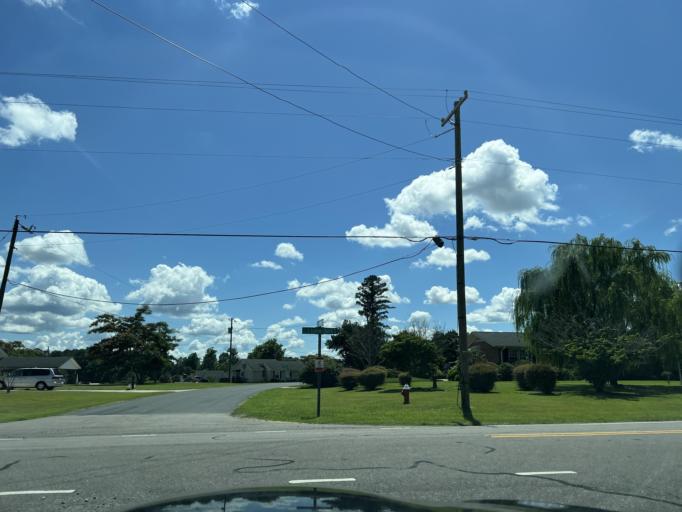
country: US
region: North Carolina
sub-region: Lee County
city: Sanford
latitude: 35.4308
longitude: -79.1609
